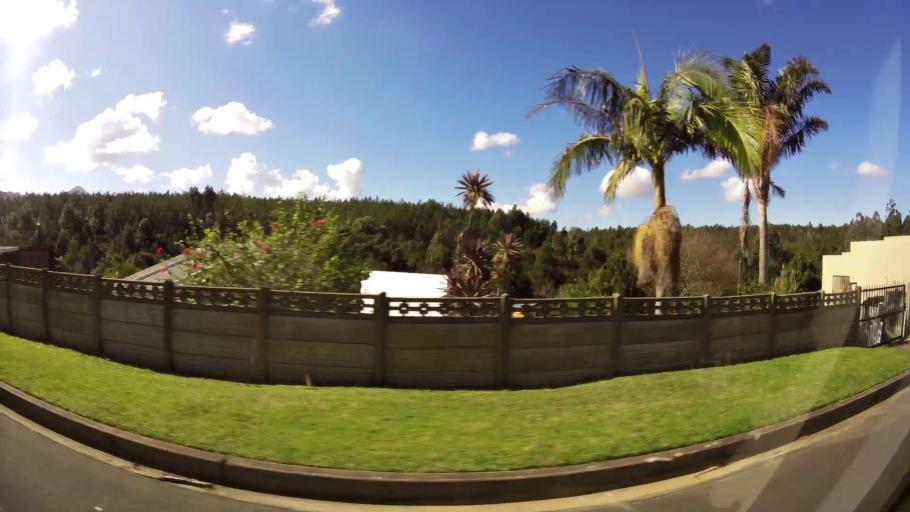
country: ZA
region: Western Cape
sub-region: Eden District Municipality
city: George
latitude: -33.9475
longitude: 22.4810
